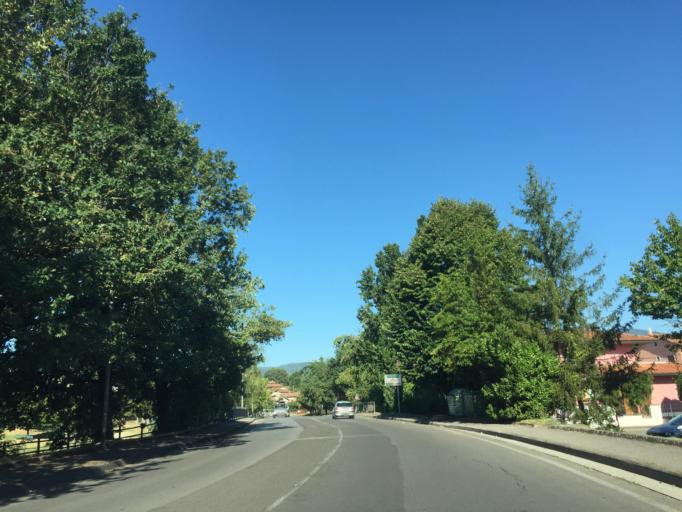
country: IT
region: Tuscany
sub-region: Provincia di Pistoia
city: Pistoia
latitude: 43.9440
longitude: 10.9144
